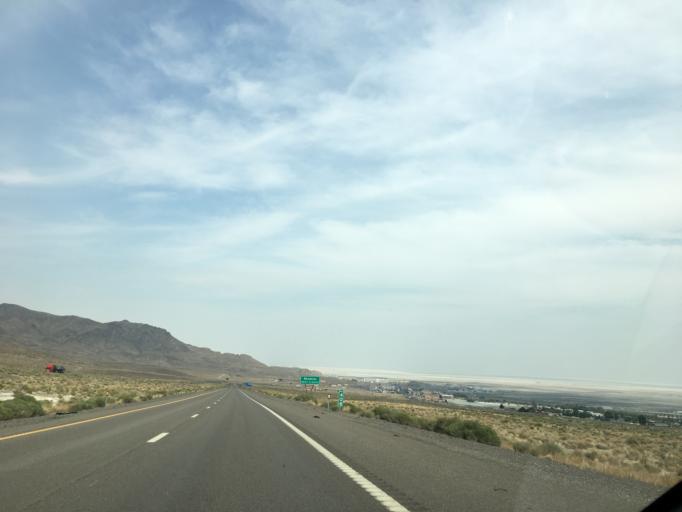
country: US
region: Nevada
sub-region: Elko County
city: West Wendover
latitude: 40.7440
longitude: -114.0927
